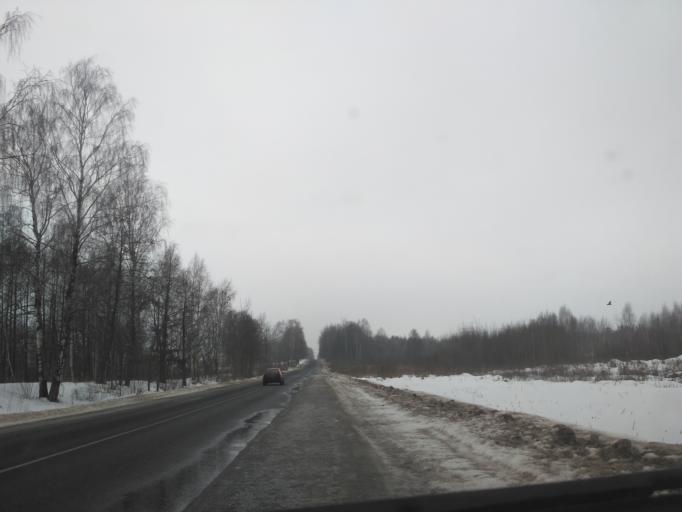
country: BY
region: Minsk
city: Horad Zhodzina
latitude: 54.0825
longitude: 28.3142
